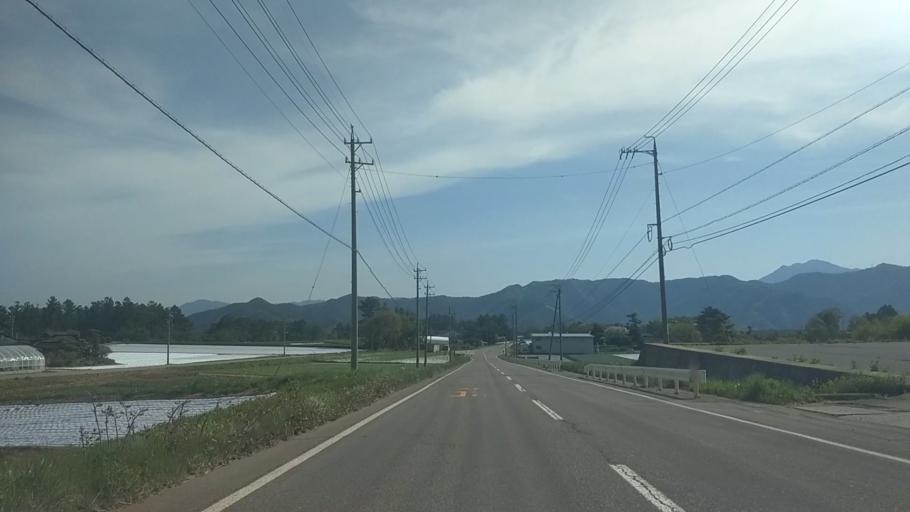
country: JP
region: Nagano
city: Saku
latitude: 35.9940
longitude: 138.4939
